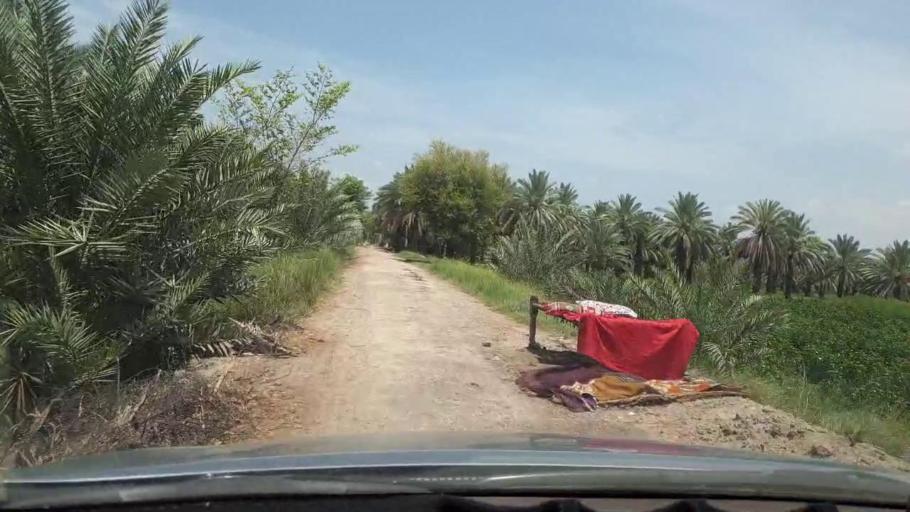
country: PK
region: Sindh
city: Khairpur
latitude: 27.4491
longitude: 68.7791
